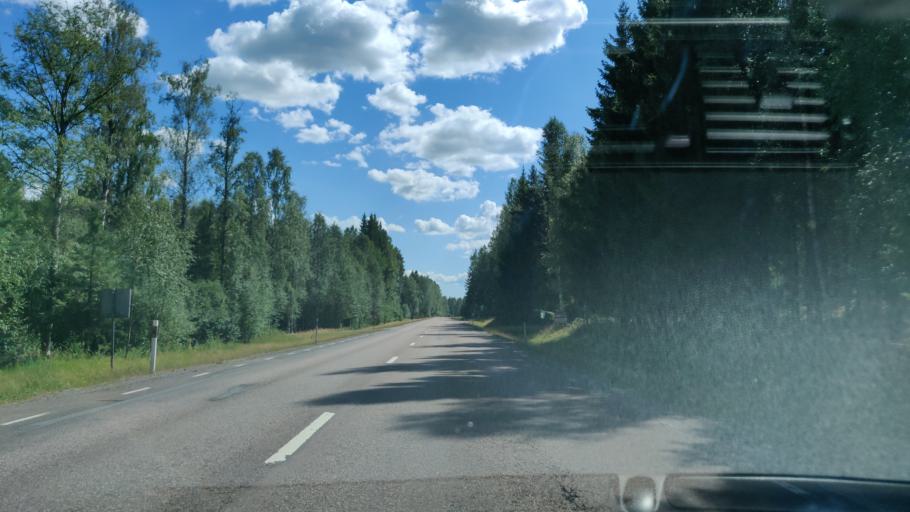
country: SE
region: Vaermland
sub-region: Hagfors Kommun
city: Ekshaerad
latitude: 60.2005
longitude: 13.4941
